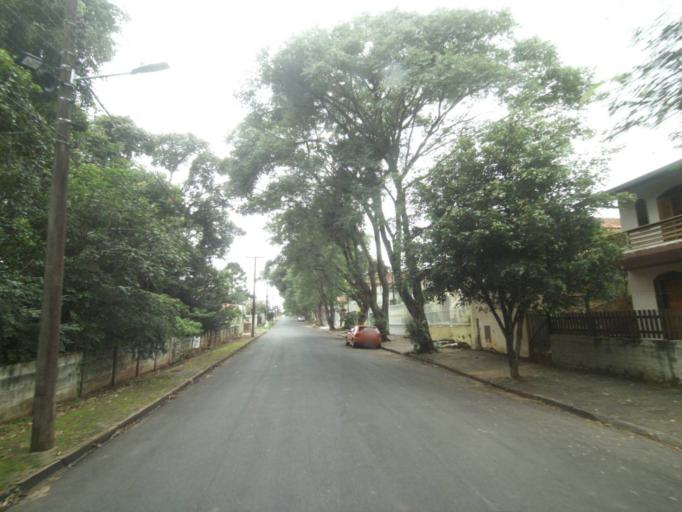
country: BR
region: Parana
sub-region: Telemaco Borba
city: Telemaco Borba
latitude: -24.3288
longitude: -50.6131
